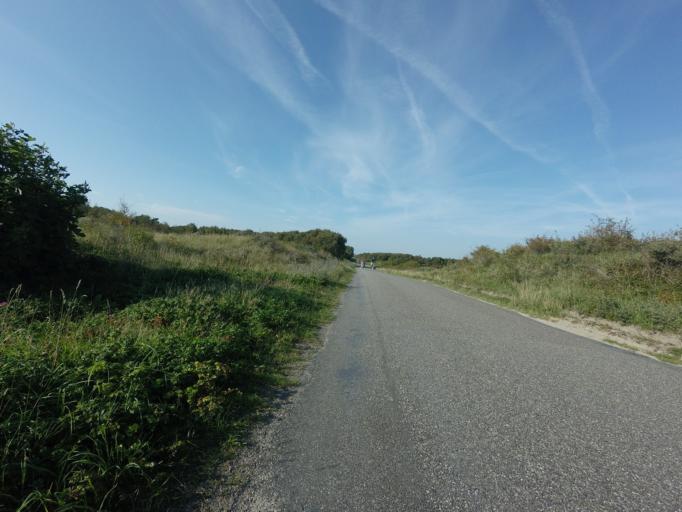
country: NL
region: Friesland
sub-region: Gemeente Schiermonnikoog
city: Schiermonnikoog
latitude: 53.4917
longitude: 6.1842
